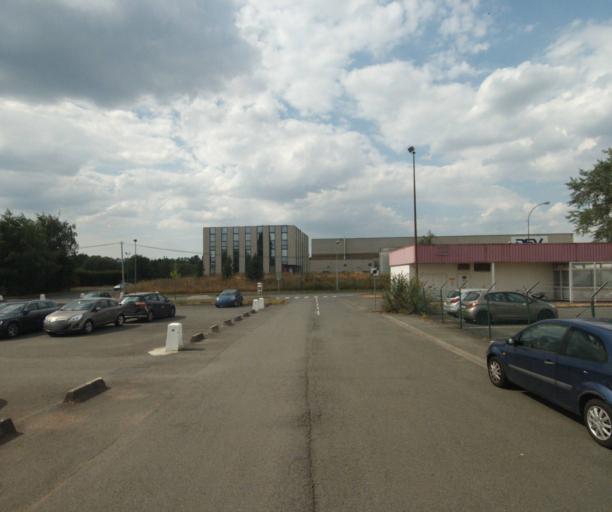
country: FR
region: Nord-Pas-de-Calais
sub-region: Departement du Nord
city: Neuville-en-Ferrain
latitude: 50.7548
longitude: 3.1581
